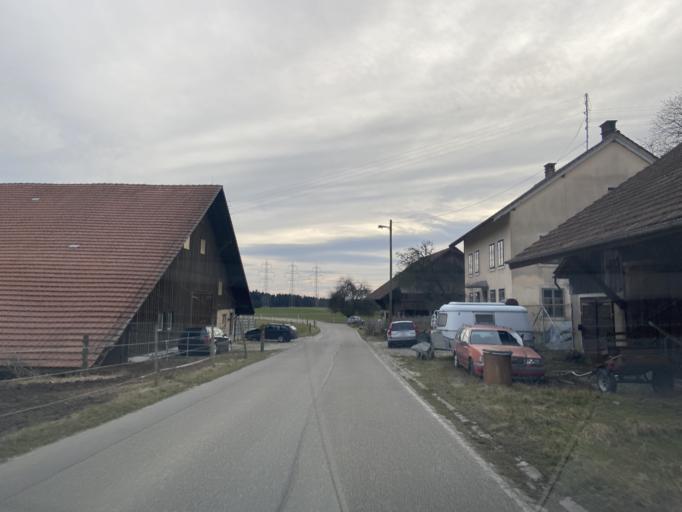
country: CH
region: Zurich
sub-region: Bezirk Winterthur
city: Brutten
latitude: 47.4885
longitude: 8.6587
